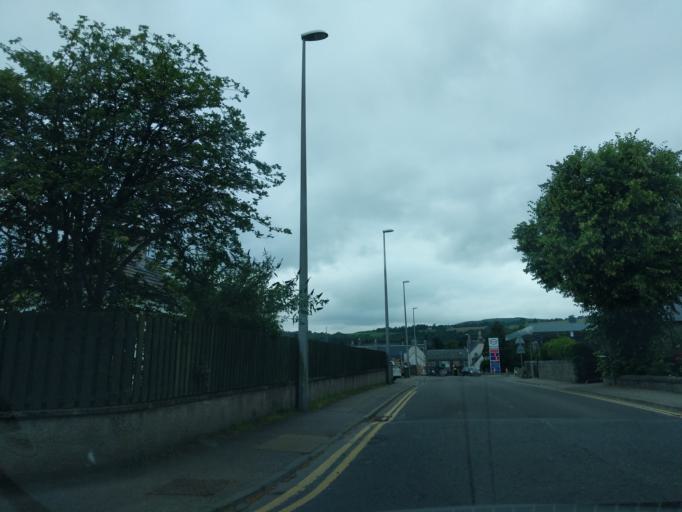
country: GB
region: Scotland
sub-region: Highland
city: Grantown on Spey
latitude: 57.3285
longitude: -3.6080
